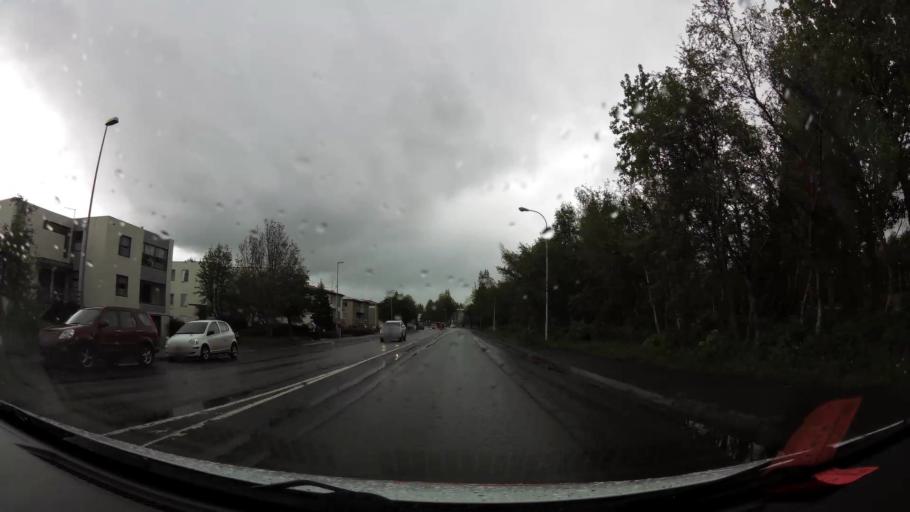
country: IS
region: Northeast
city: Akureyri
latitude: 65.6810
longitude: -18.1002
